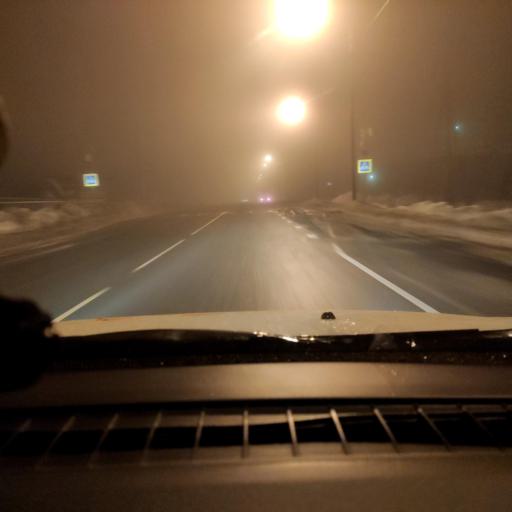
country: RU
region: Samara
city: Dubovyy Umet
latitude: 52.9617
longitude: 50.2911
